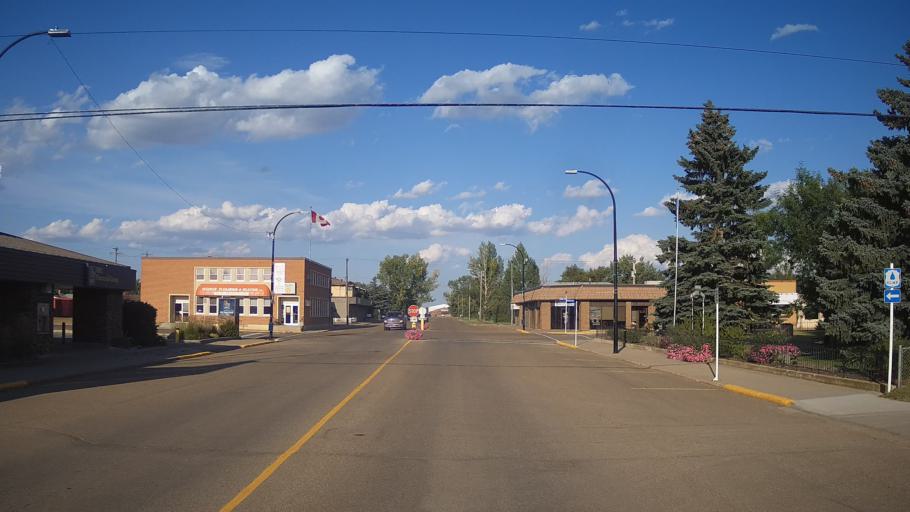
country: CA
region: Alberta
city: Hanna
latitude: 51.6434
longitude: -111.9264
